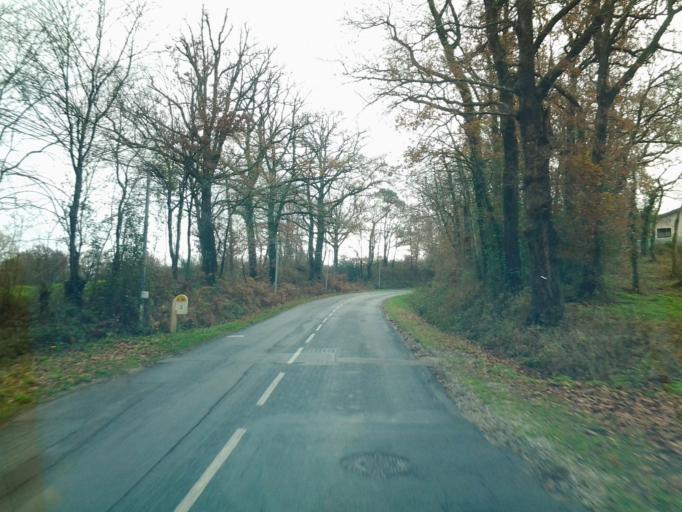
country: FR
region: Pays de la Loire
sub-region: Departement de la Vendee
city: La Roche-sur-Yon
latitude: 46.6586
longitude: -1.3973
